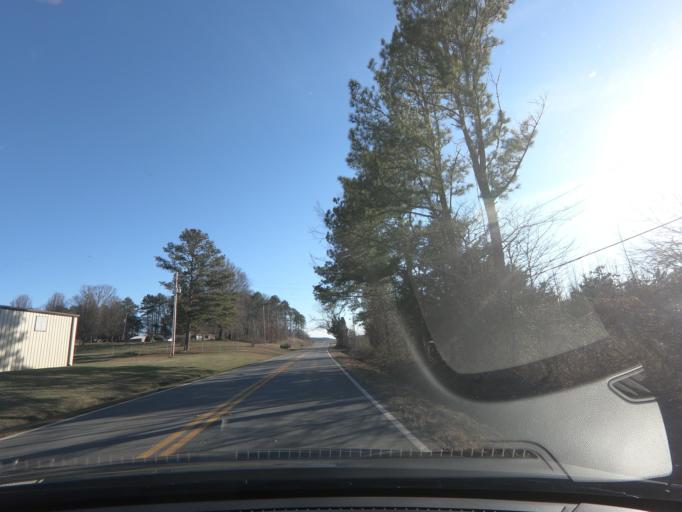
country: US
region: Georgia
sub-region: Gordon County
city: Calhoun
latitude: 34.4496
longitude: -84.9143
